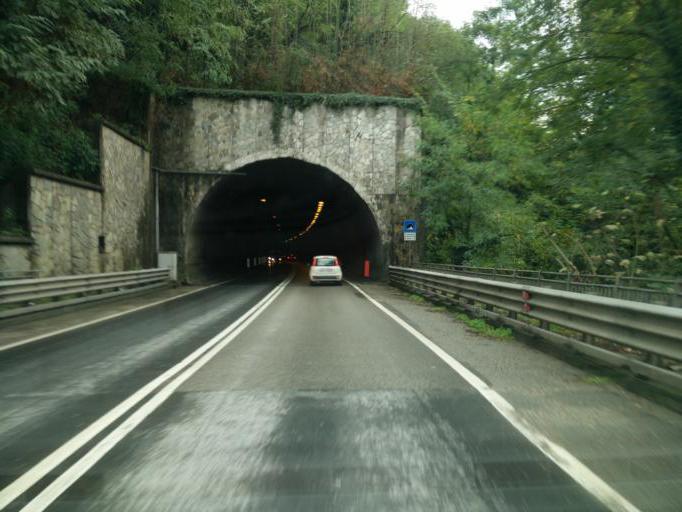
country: IT
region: Tuscany
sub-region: Provincia di Lucca
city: Valdottavo
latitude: 43.9115
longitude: 10.5244
